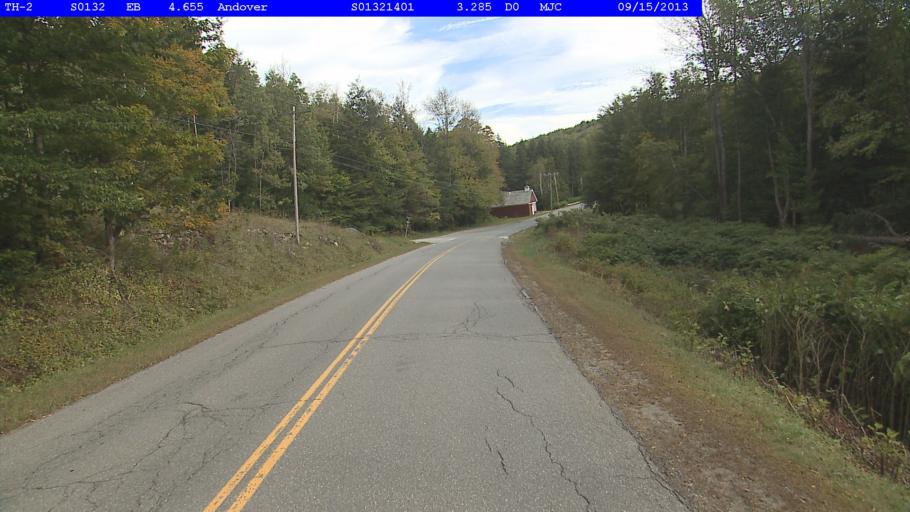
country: US
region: Vermont
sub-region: Windsor County
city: Chester
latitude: 43.2823
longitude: -72.7080
